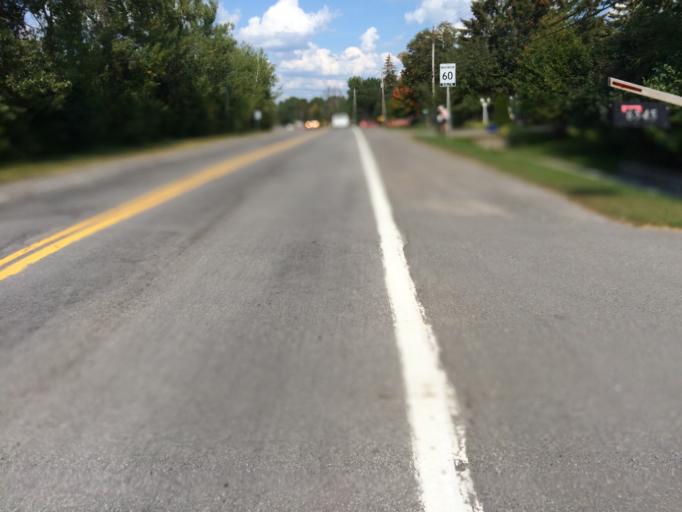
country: CA
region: Ontario
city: Bells Corners
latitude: 45.1655
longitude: -75.6415
